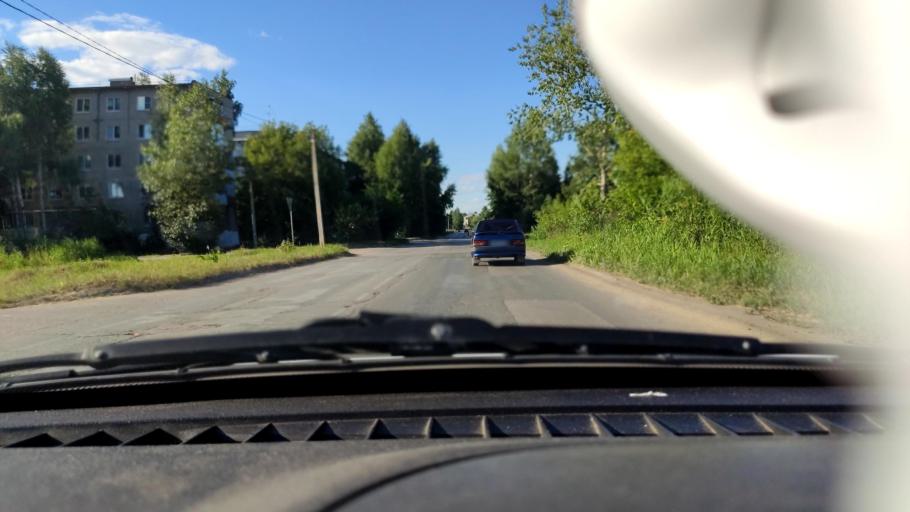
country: RU
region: Perm
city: Krasnokamsk
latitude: 58.0848
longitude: 55.7855
